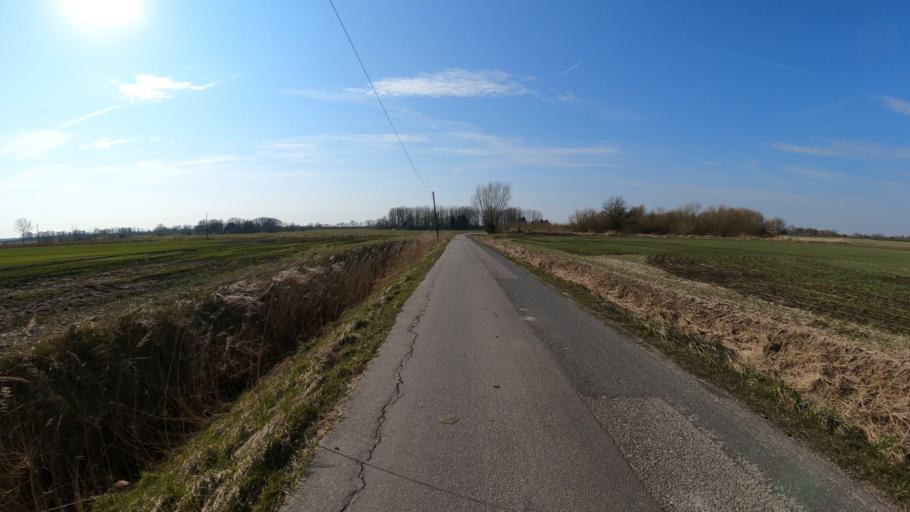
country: DE
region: Schleswig-Holstein
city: Seestermuhe
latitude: 53.7121
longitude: 9.5379
